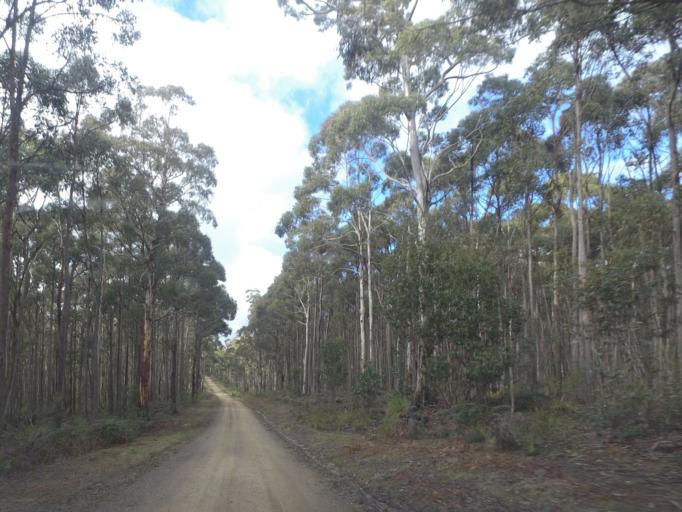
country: AU
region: Victoria
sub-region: Moorabool
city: Bacchus Marsh
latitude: -37.4228
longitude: 144.4179
